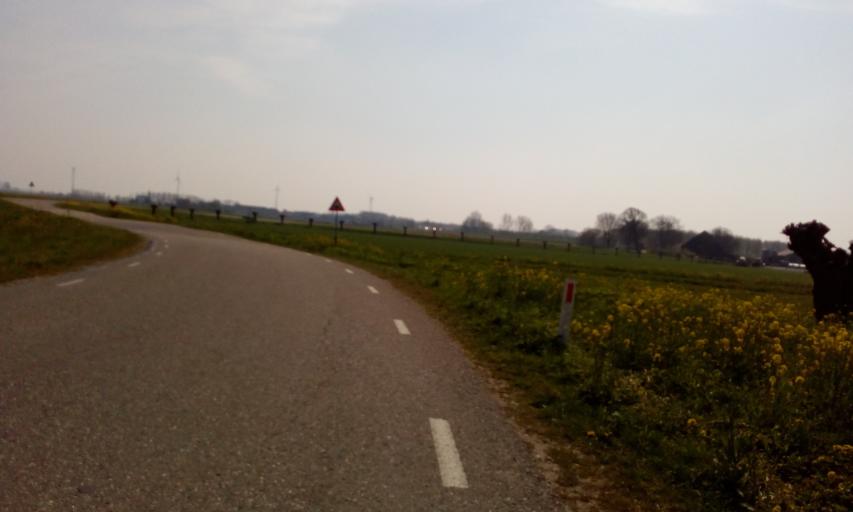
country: NL
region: South Holland
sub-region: Gemeente Spijkenisse
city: Spijkenisse
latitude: 51.8310
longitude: 4.2810
